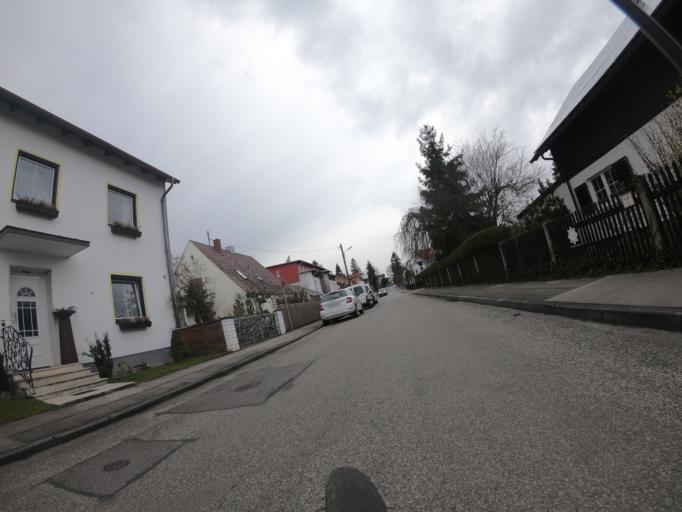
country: DE
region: Bavaria
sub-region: Upper Bavaria
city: Fuerstenfeldbruck
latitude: 48.1725
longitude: 11.2394
